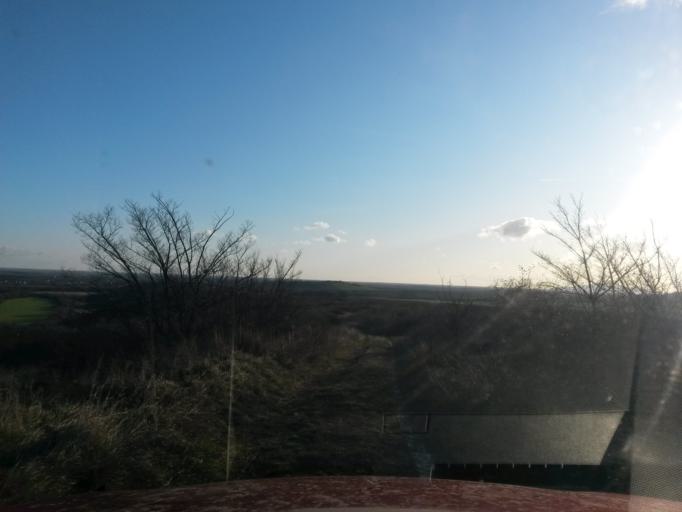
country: HU
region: Borsod-Abauj-Zemplen
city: Sarospatak
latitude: 48.3271
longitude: 21.5381
